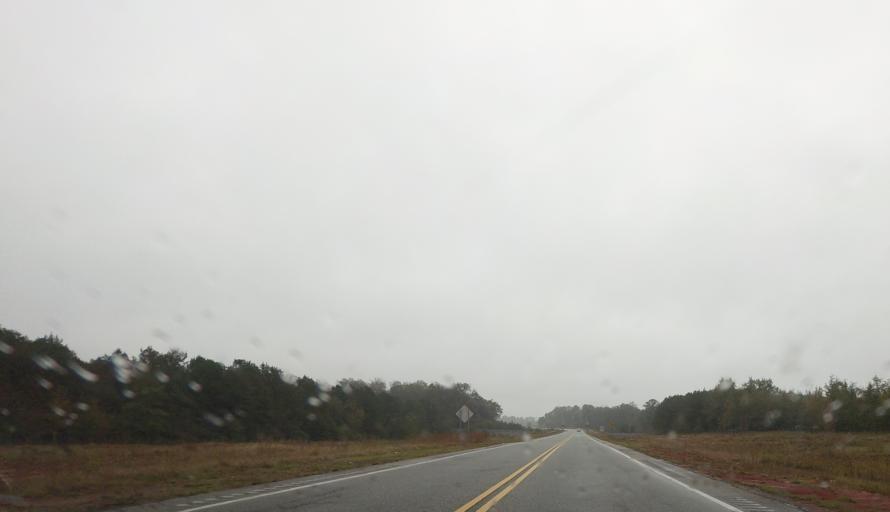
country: US
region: Georgia
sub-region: Peach County
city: Fort Valley
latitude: 32.5383
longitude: -83.9072
